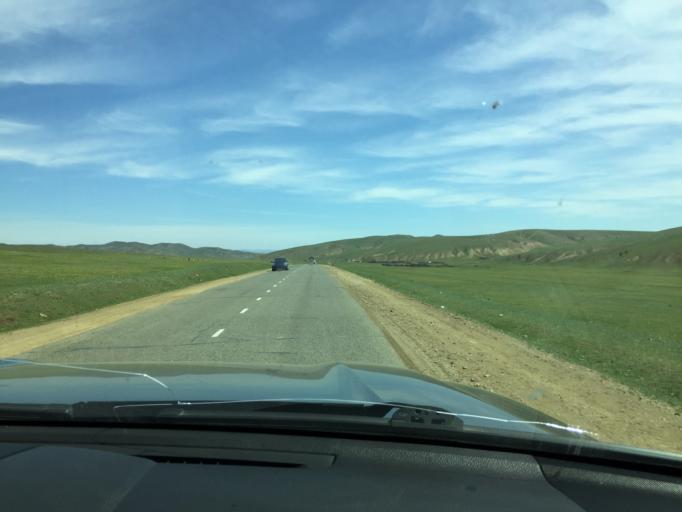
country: MN
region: Central Aimak
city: Bornuur
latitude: 48.6610
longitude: 106.1222
